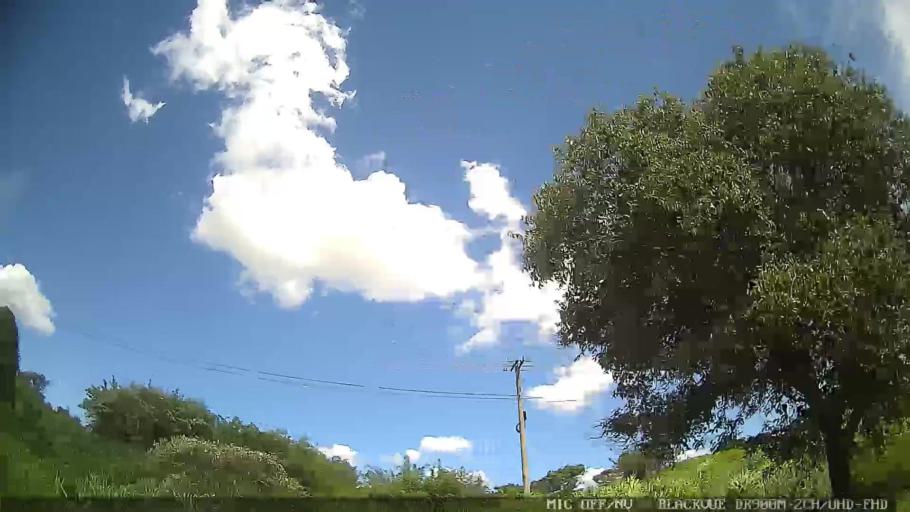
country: BR
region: Sao Paulo
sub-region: Pedreira
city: Pedreira
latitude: -22.7159
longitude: -46.8399
